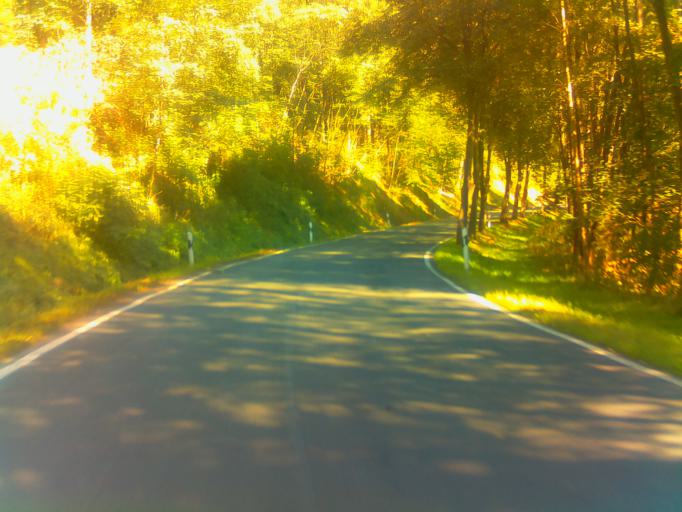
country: DE
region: Thuringia
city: Waltersdorf
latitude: 50.8338
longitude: 11.7556
